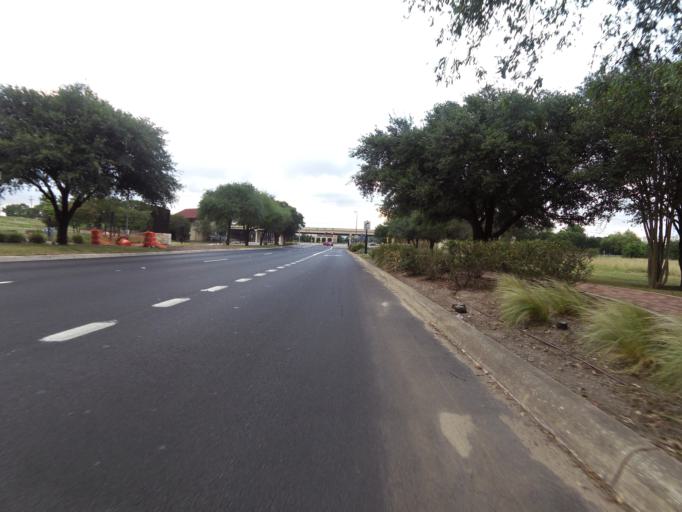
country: US
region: Texas
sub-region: Bexar County
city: Shavano Park
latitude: 29.6044
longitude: -98.6035
